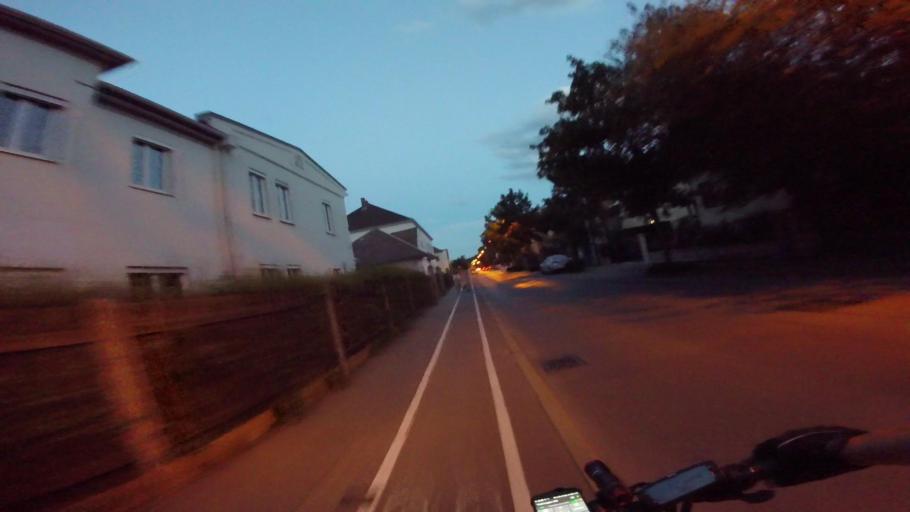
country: AT
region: Lower Austria
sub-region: Politischer Bezirk Modling
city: Modling
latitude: 48.0807
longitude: 16.2948
